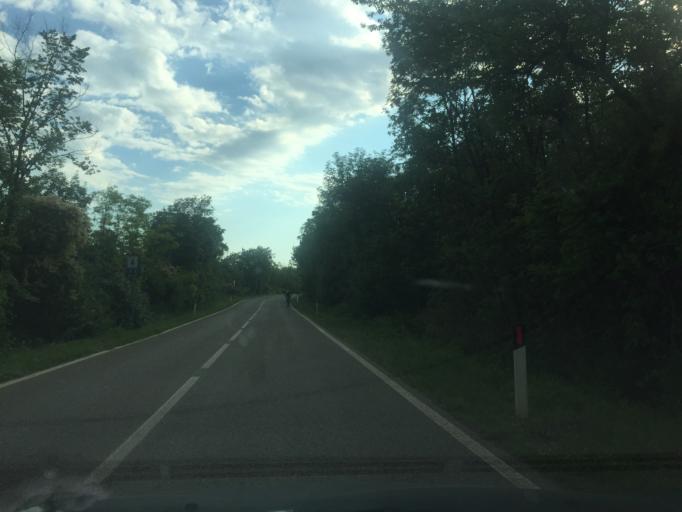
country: IT
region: Friuli Venezia Giulia
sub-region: Provincia di Gorizia
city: Doberdo del Lago
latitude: 45.8729
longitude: 13.5303
